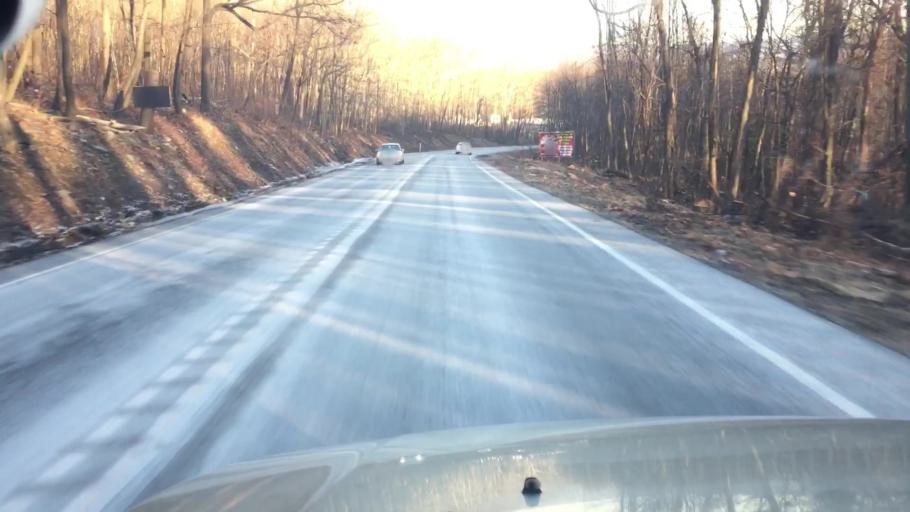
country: US
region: Pennsylvania
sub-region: Luzerne County
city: Conyngham
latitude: 41.0311
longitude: -76.0839
